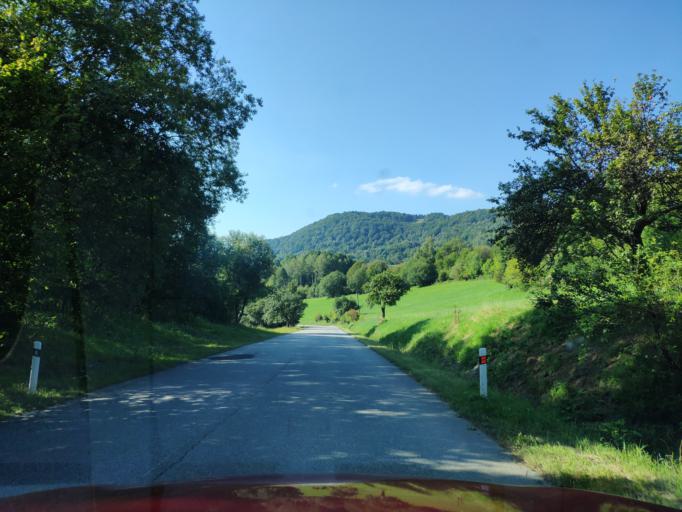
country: PL
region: Subcarpathian Voivodeship
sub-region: Powiat leski
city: Cisna
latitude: 49.0504
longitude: 22.3061
